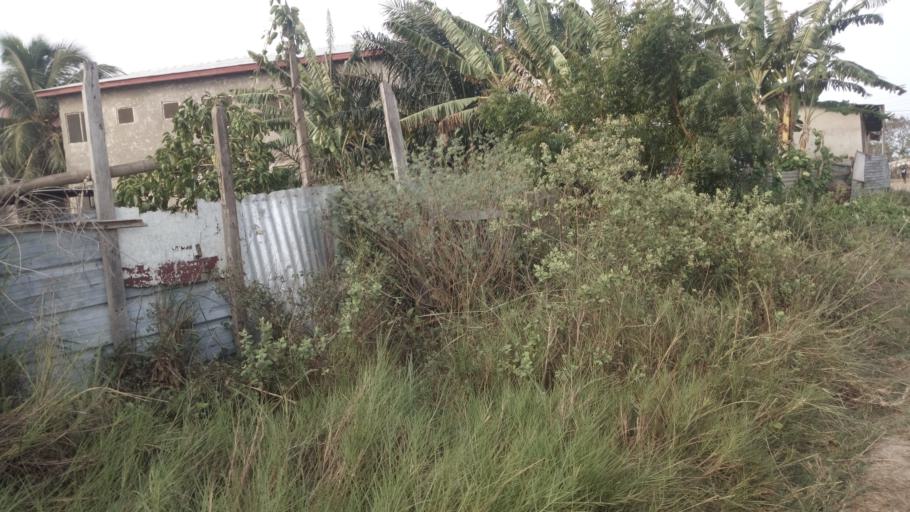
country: GH
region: Central
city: Winneba
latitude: 5.3497
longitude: -0.6349
